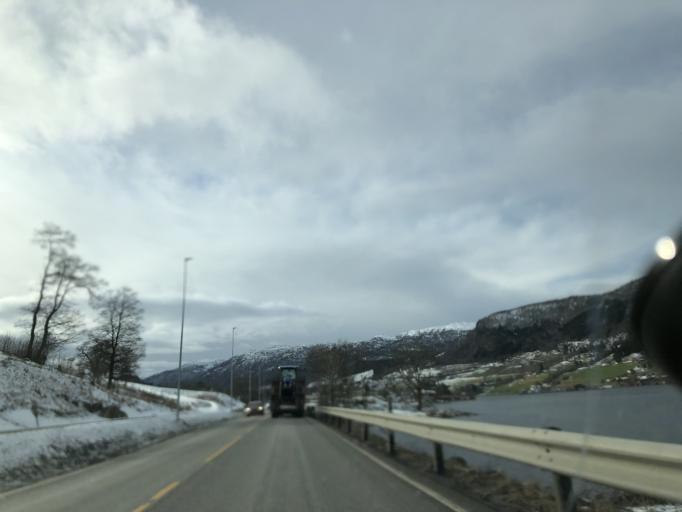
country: NO
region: Rogaland
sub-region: Vindafjord
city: Olen
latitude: 59.6000
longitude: 5.7685
